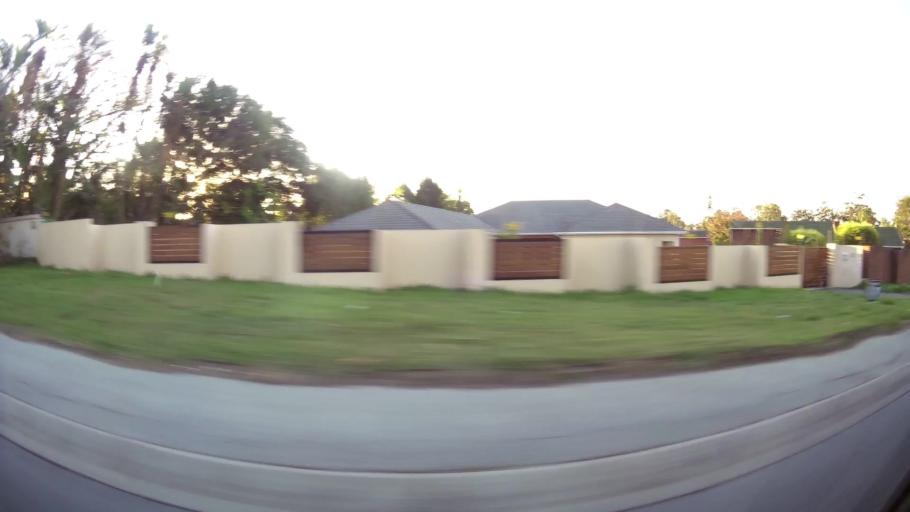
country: ZA
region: Eastern Cape
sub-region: Nelson Mandela Bay Metropolitan Municipality
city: Port Elizabeth
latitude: -33.9626
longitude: 25.5057
